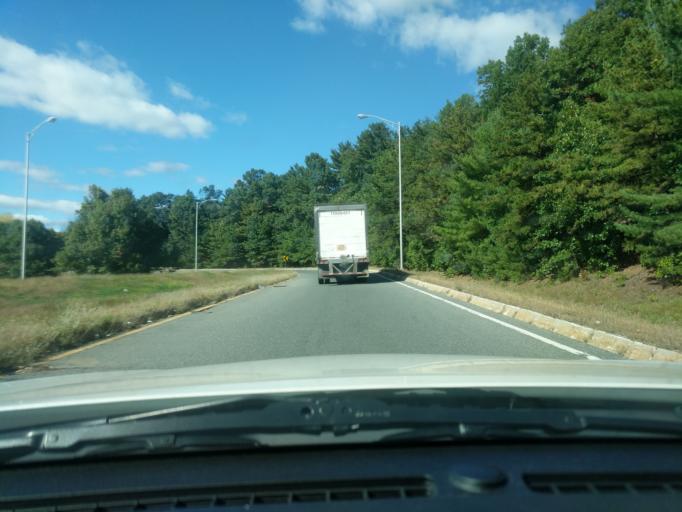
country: US
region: Massachusetts
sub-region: Hampden County
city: Westfield
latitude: 42.1455
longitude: -72.7332
